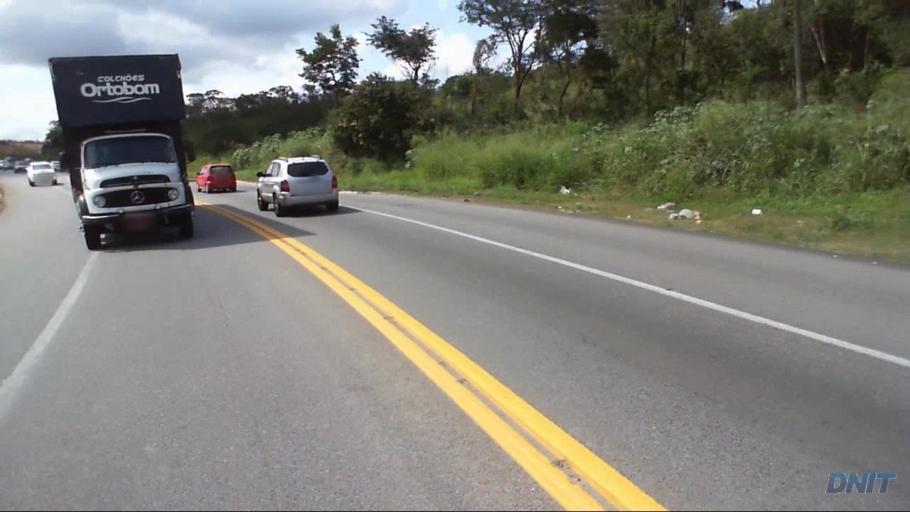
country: BR
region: Minas Gerais
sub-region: Santa Luzia
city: Santa Luzia
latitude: -19.8180
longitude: -43.8111
